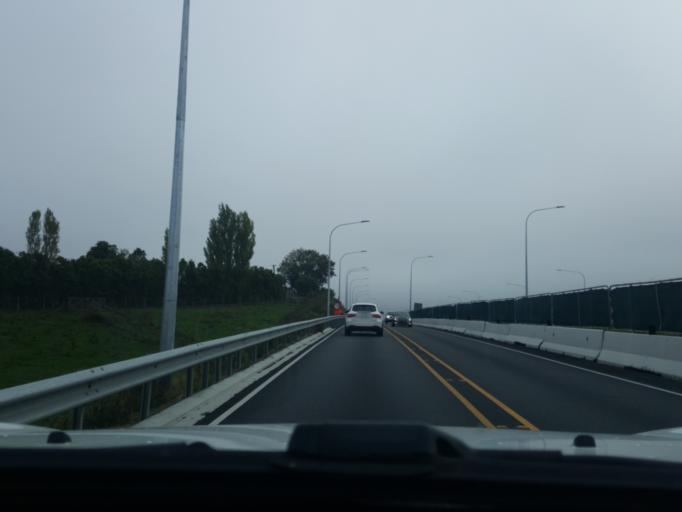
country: NZ
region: Waikato
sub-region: Waikato District
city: Te Kauwhata
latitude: -37.5094
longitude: 175.1663
